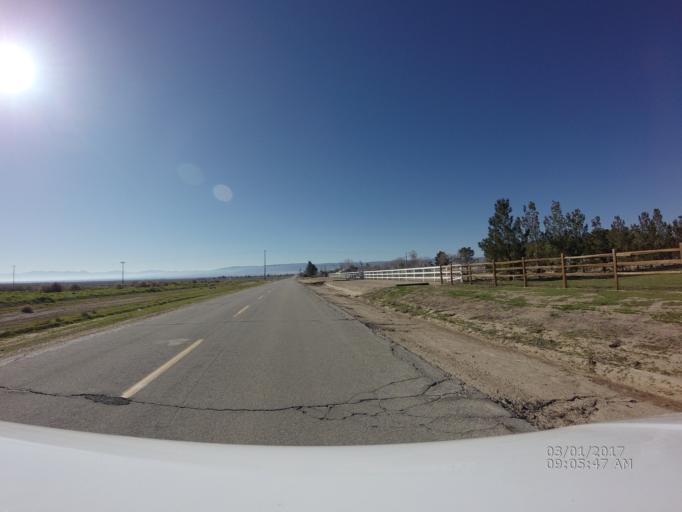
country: US
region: California
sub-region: Los Angeles County
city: Quartz Hill
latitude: 34.7630
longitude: -118.2724
